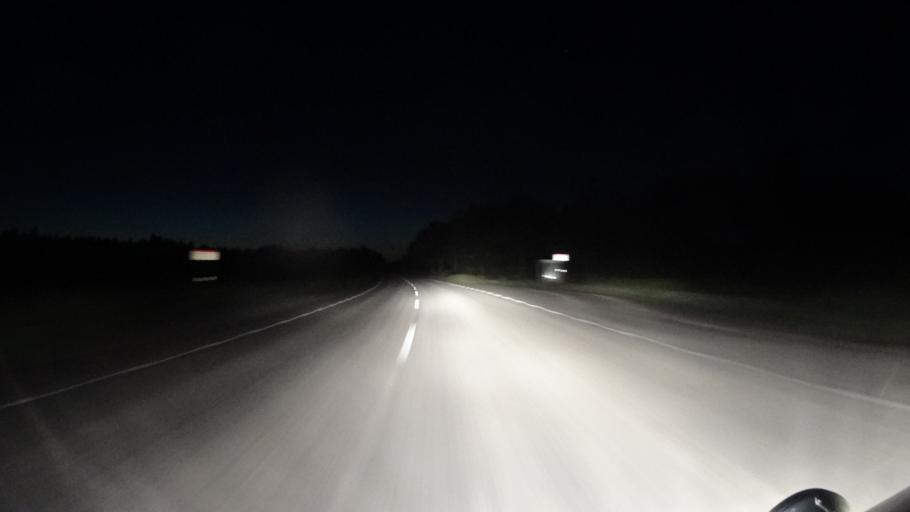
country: SE
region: OEstergoetland
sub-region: Odeshogs Kommun
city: OEdeshoeg
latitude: 58.2762
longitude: 14.7567
